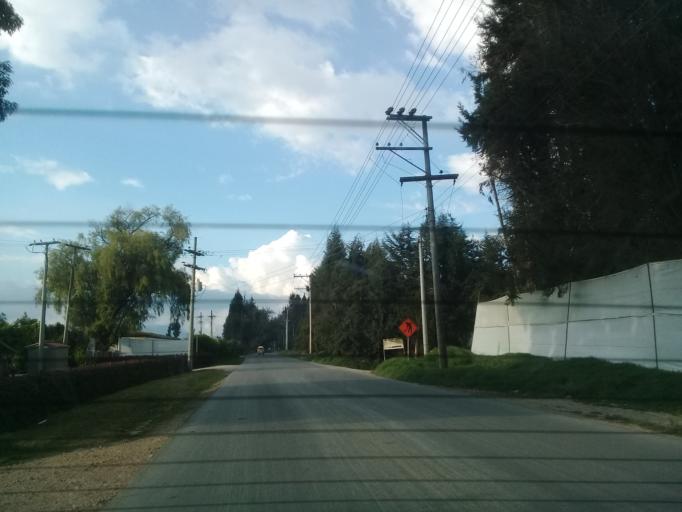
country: CO
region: Cundinamarca
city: Madrid
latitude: 4.7601
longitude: -74.2643
